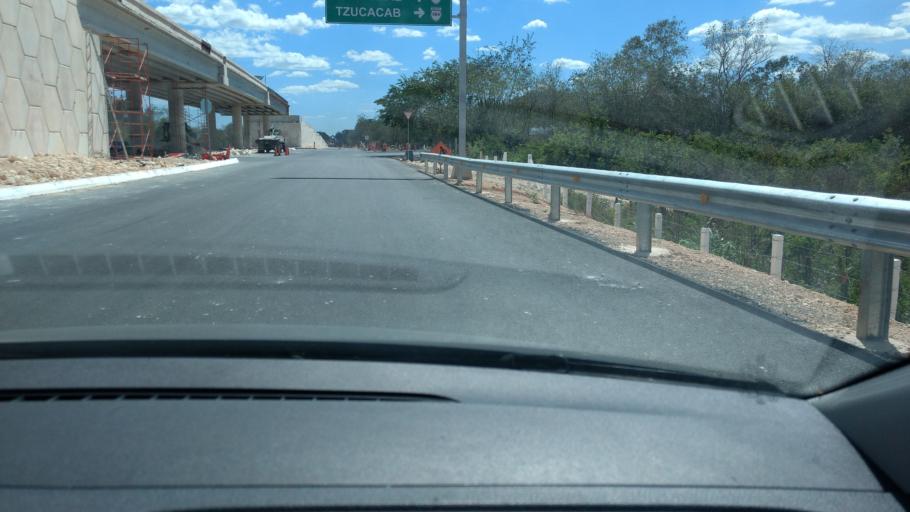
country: MX
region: Yucatan
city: Peto
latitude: 20.1197
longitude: -88.9481
